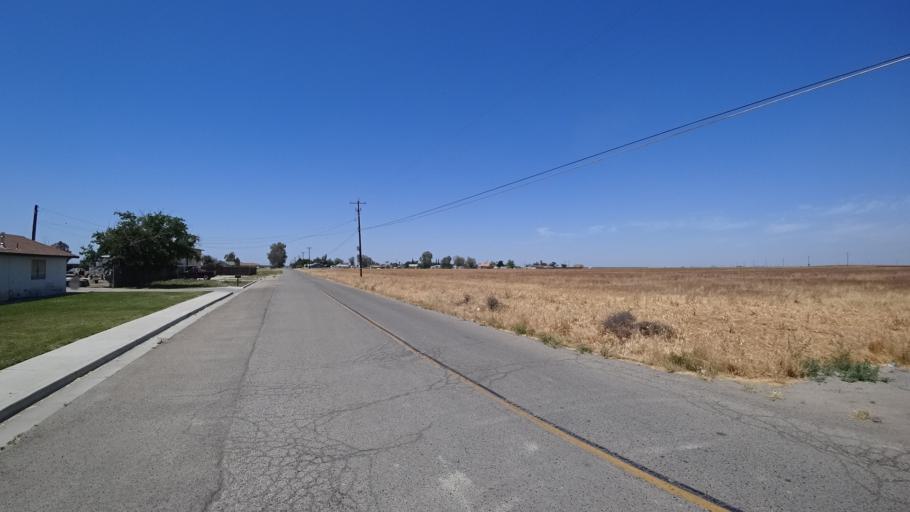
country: US
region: California
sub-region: Kings County
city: Corcoran
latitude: 36.1162
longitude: -119.5724
